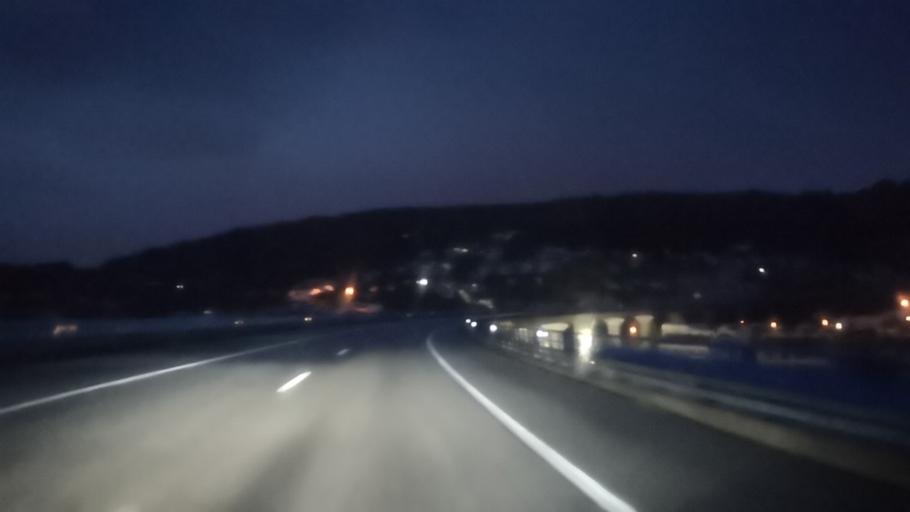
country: PT
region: Braga
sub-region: Guimaraes
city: Candoso
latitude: 41.4090
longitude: -8.3168
